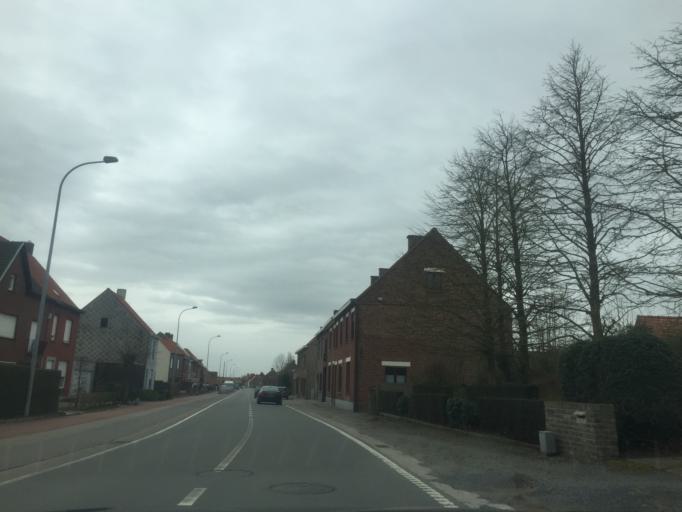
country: BE
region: Flanders
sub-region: Provincie West-Vlaanderen
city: Izegem
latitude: 50.9379
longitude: 3.2055
